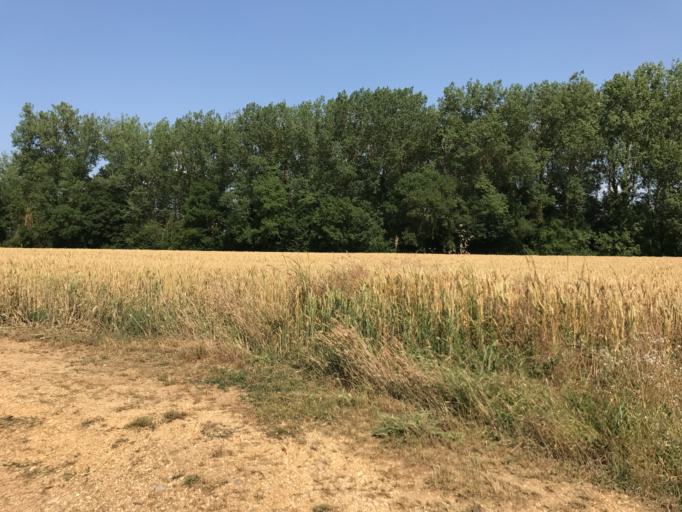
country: ES
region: Basque Country
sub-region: Provincia de Alava
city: Gasteiz / Vitoria
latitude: 42.8800
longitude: -2.6452
